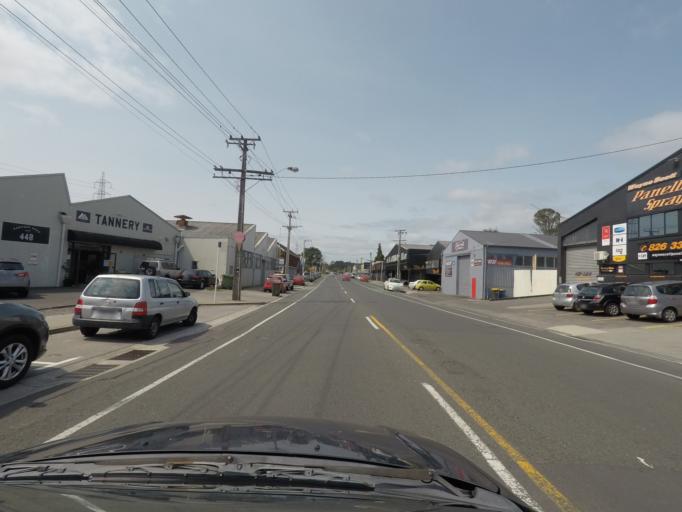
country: NZ
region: Auckland
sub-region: Auckland
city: Waitakere
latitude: -36.9130
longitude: 174.6901
